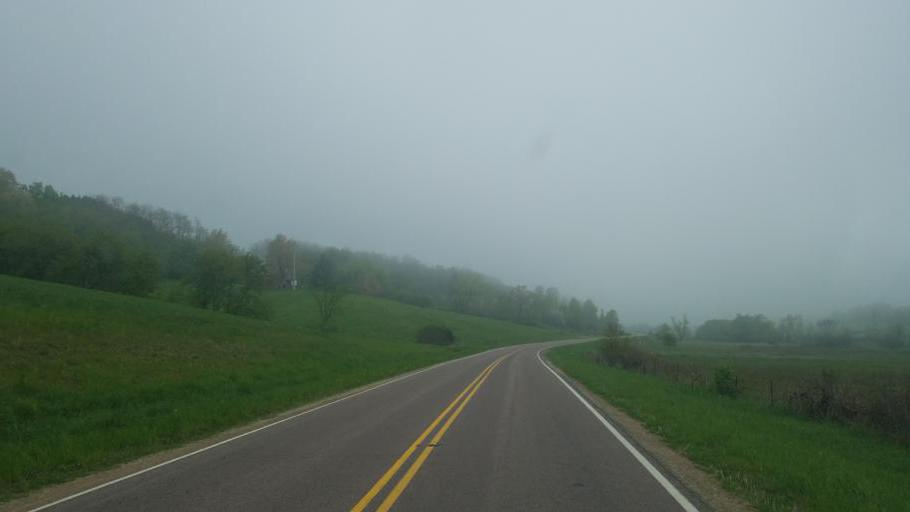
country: US
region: Wisconsin
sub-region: Vernon County
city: Hillsboro
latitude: 43.6222
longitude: -90.3478
